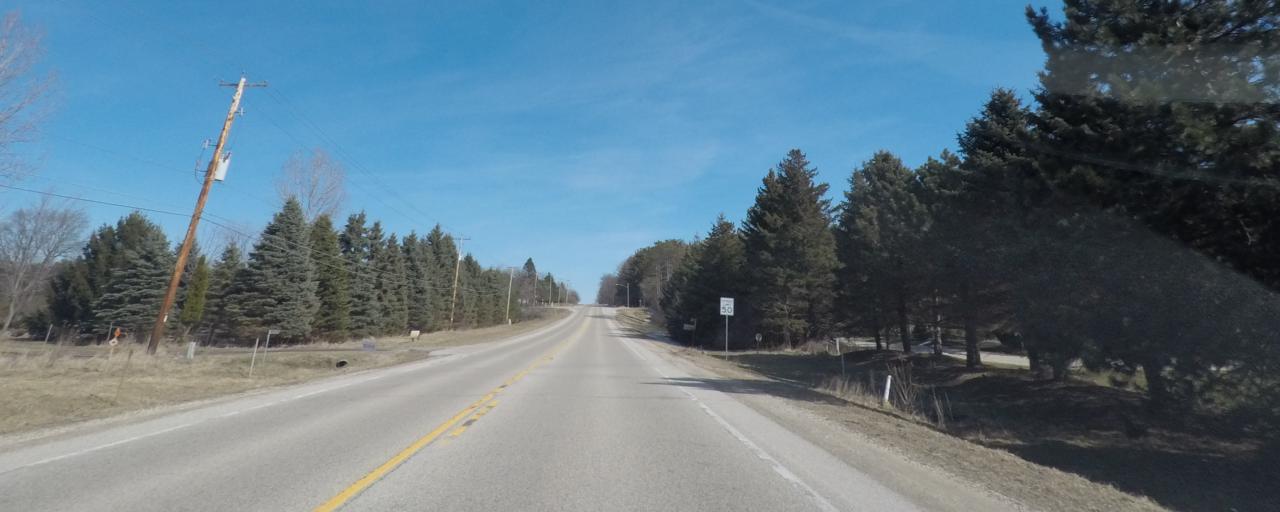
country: US
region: Wisconsin
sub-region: Waukesha County
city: Merton
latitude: 43.1558
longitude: -88.3247
